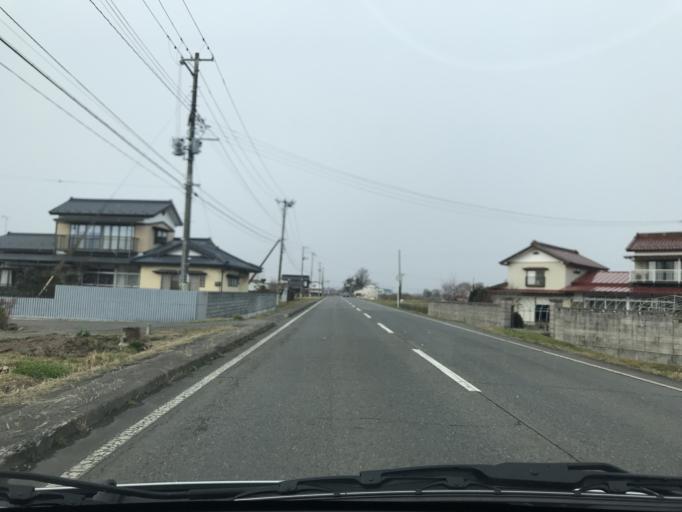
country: JP
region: Iwate
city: Mizusawa
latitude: 39.1770
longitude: 141.1368
